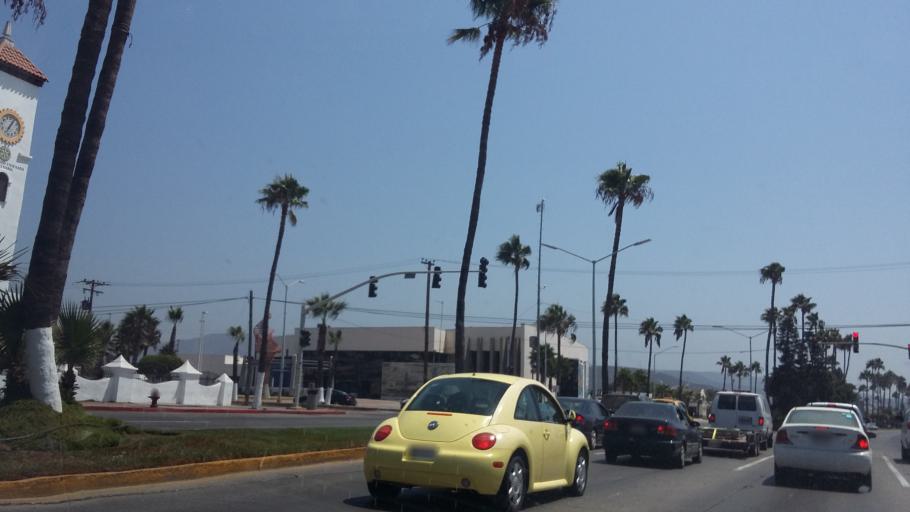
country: MX
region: Baja California
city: Ensenada
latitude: 31.8573
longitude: -116.6194
